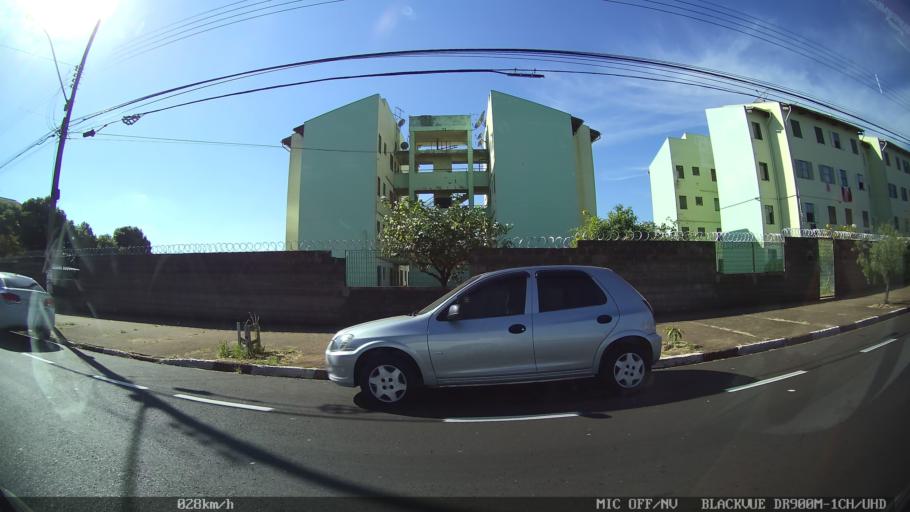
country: BR
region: Sao Paulo
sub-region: Franca
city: Franca
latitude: -20.4973
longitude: -47.4197
